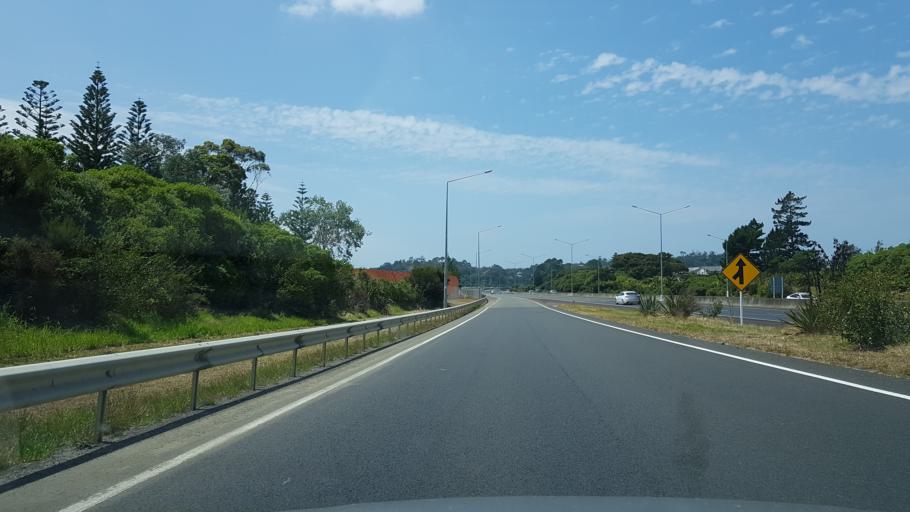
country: NZ
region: Auckland
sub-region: Auckland
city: Rosebank
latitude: -36.7899
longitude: 174.6560
